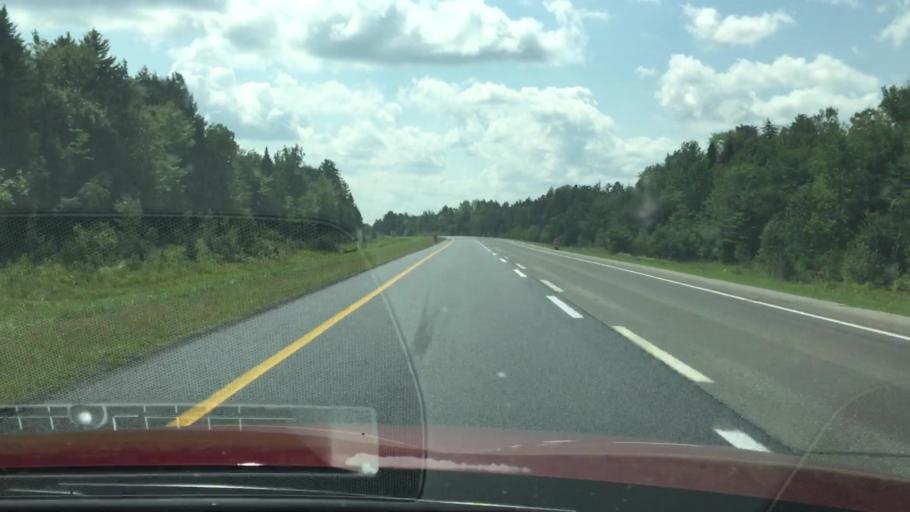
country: US
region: Maine
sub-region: Penobscot County
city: Medway
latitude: 45.7044
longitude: -68.4819
